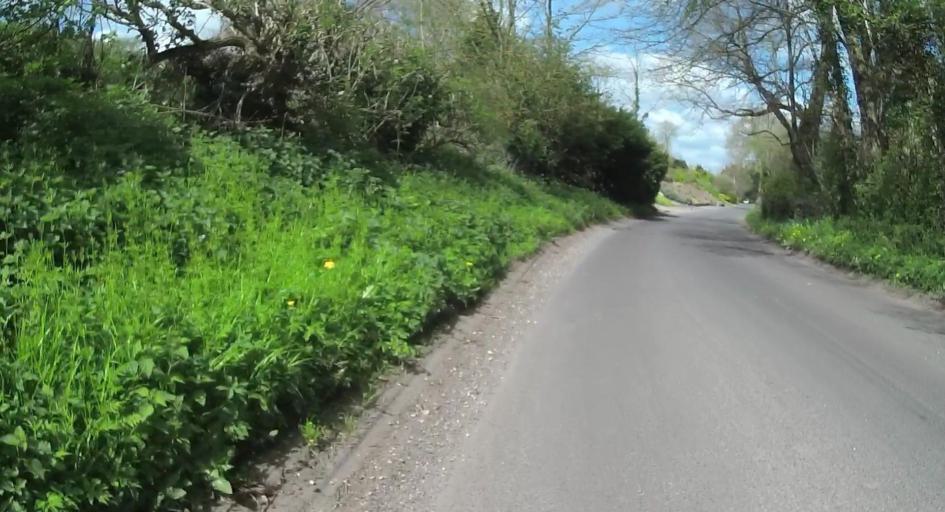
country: GB
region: England
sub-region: Hampshire
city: Abbotts Ann
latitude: 51.1119
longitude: -1.4996
